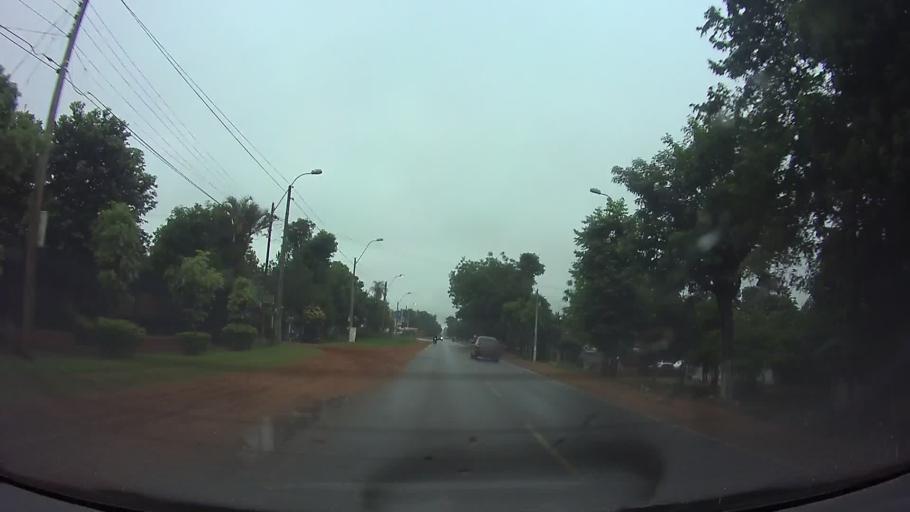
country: PY
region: Central
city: Ita
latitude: -25.4969
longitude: -57.3581
